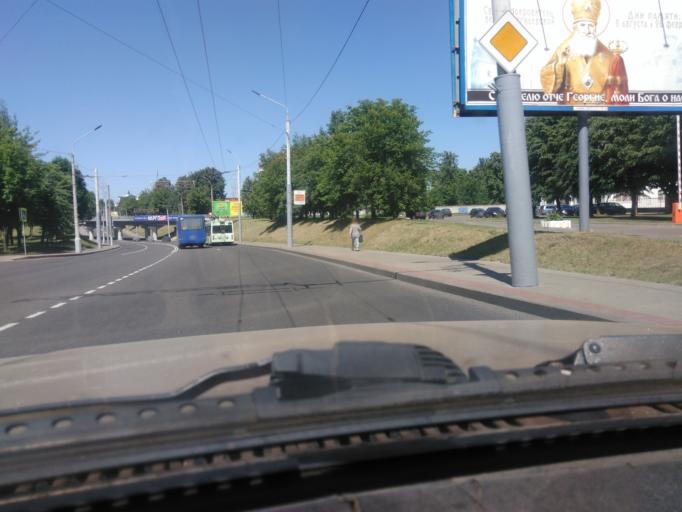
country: BY
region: Mogilev
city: Mahilyow
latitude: 53.9207
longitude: 30.3431
